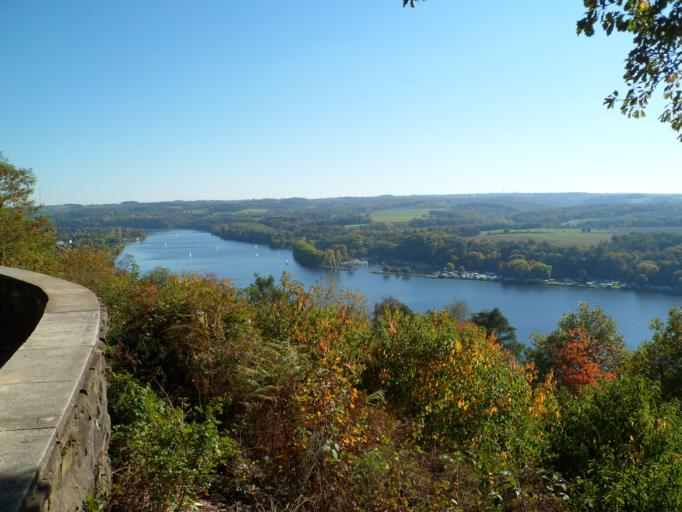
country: DE
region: North Rhine-Westphalia
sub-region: Regierungsbezirk Dusseldorf
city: Essen
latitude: 51.4084
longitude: 7.0414
